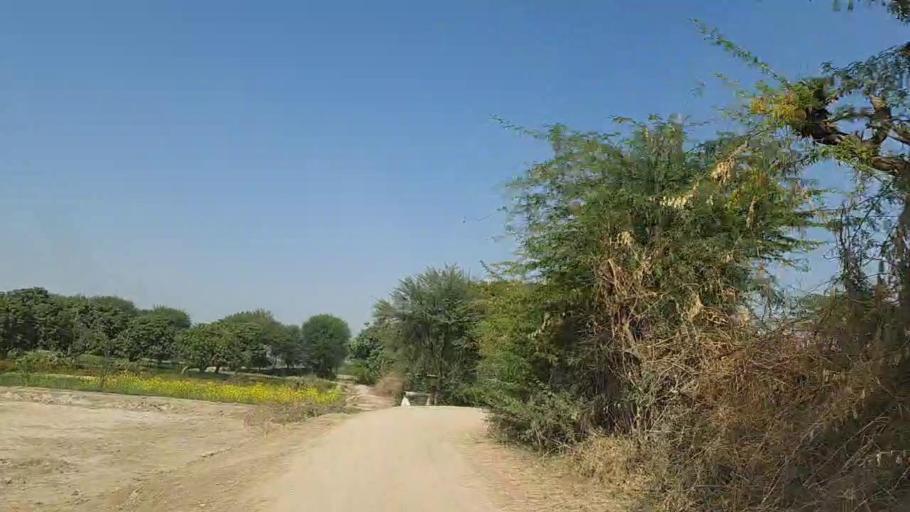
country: PK
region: Sindh
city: Naukot
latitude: 24.8577
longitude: 69.4195
